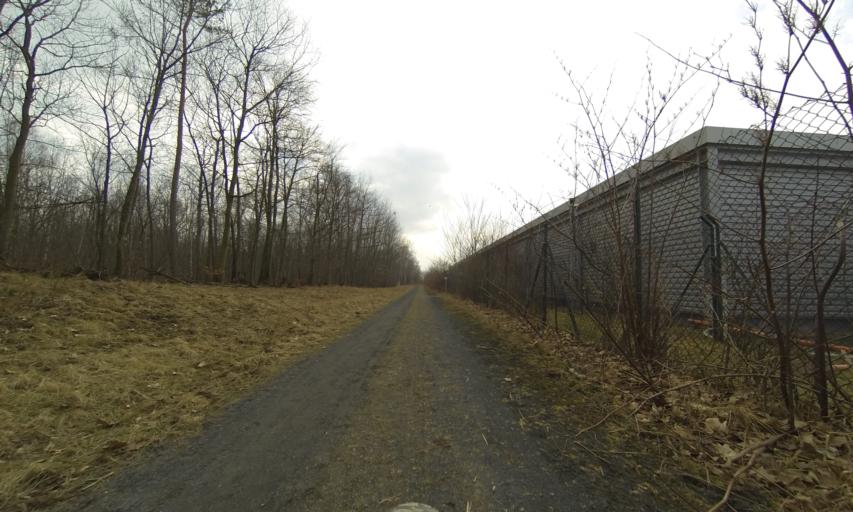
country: DE
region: Saxony
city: Albertstadt
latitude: 51.1039
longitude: 13.7798
